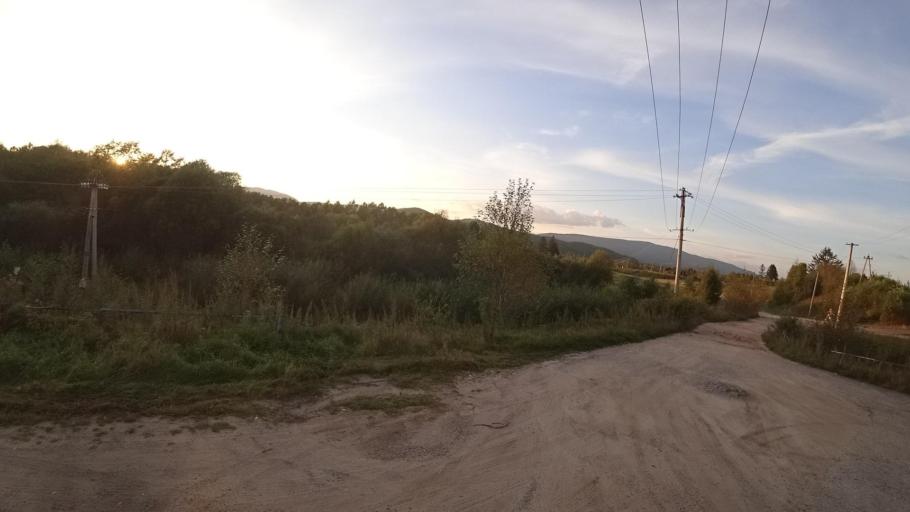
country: RU
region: Jewish Autonomous Oblast
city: Kul'dur
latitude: 49.1962
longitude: 131.6335
